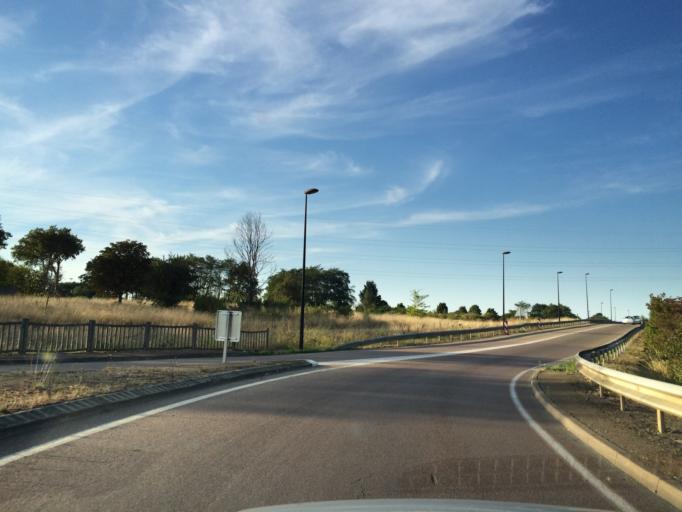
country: FR
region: Bourgogne
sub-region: Departement de l'Yonne
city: Auxerre
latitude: 47.8167
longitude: 3.5606
